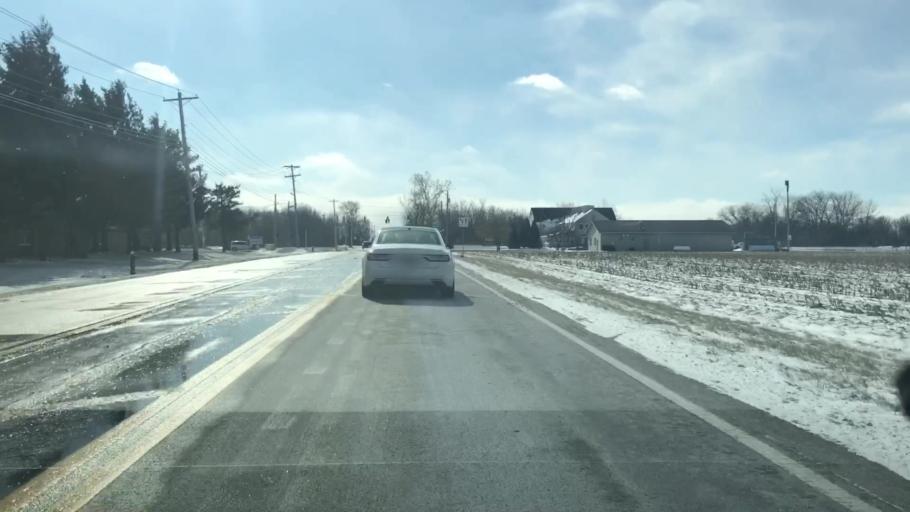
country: US
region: Ohio
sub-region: Franklin County
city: Lake Darby
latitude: 40.0012
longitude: -83.2021
